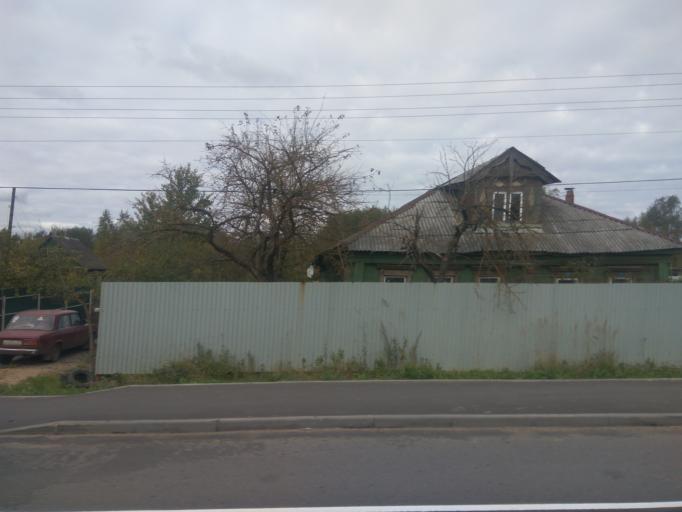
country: RU
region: Moskovskaya
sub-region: Shchelkovskiy Rayon
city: Grebnevo
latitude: 55.9818
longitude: 38.1193
